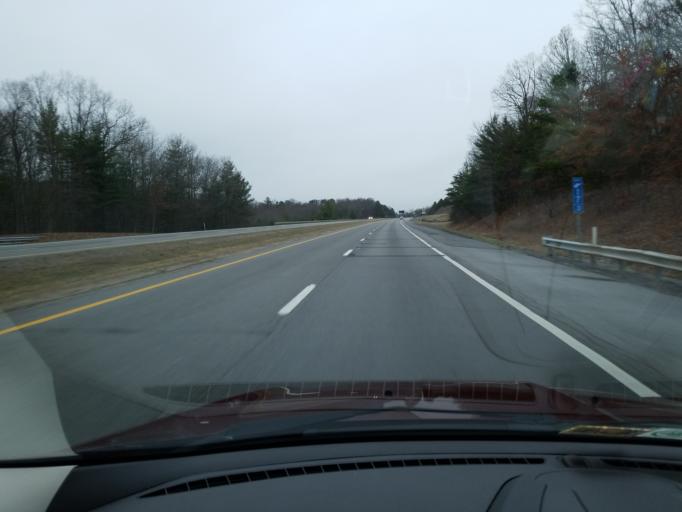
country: US
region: West Virginia
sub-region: Mercer County
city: Athens
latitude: 37.3571
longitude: -81.0232
